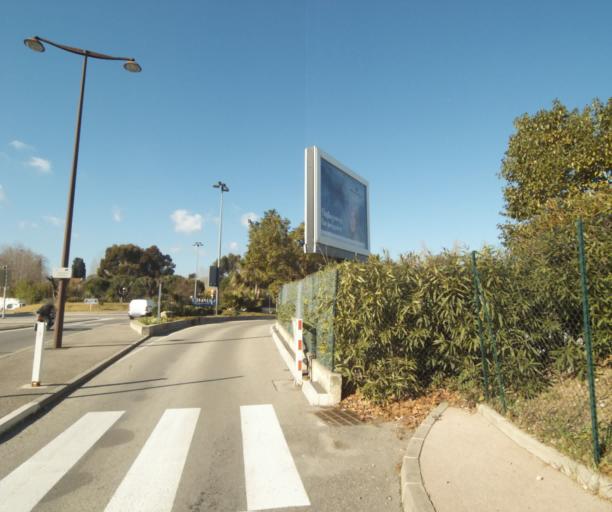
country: FR
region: Provence-Alpes-Cote d'Azur
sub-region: Departement des Alpes-Maritimes
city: Biot
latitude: 43.6146
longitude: 7.1207
